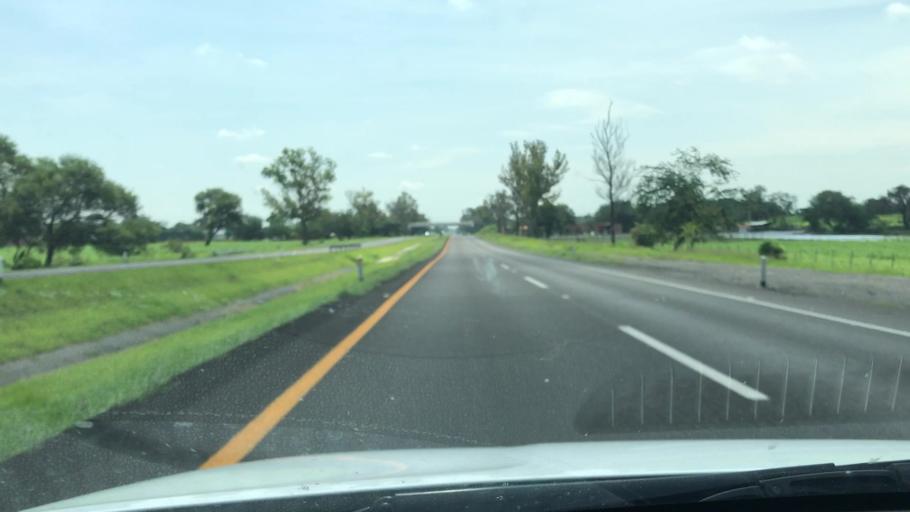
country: MX
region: Jalisco
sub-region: Ocotlan
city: Joconoxtle (La Tuna)
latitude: 20.3805
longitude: -102.6957
